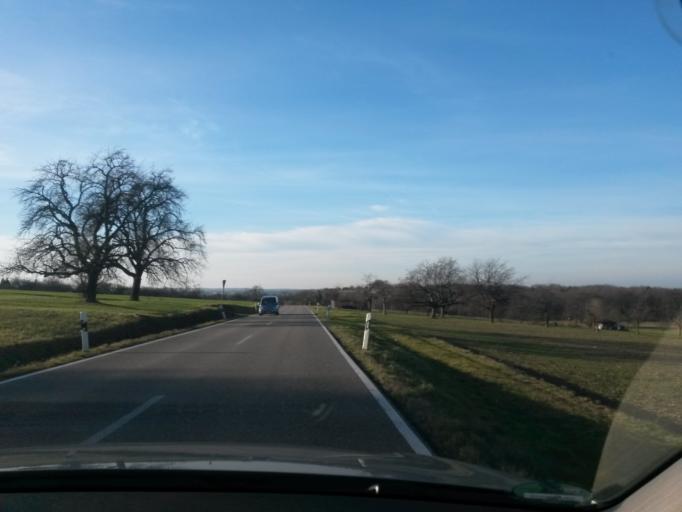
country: DE
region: Baden-Wuerttemberg
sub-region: Karlsruhe Region
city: Birkenfeld
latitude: 48.8710
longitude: 8.6138
